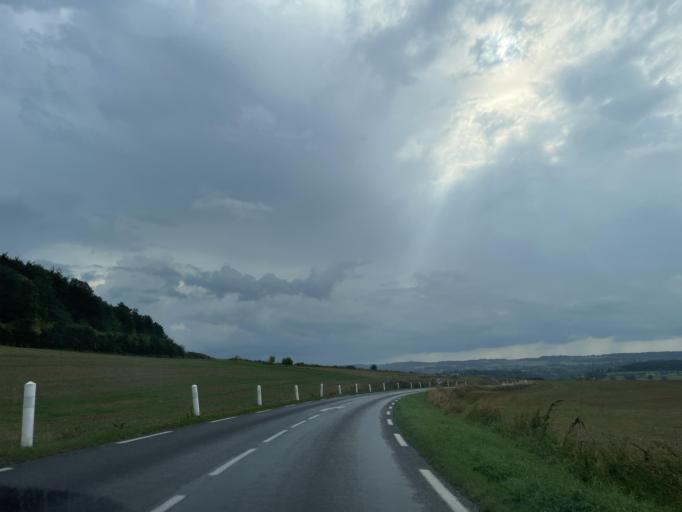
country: FR
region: Haute-Normandie
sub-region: Departement de la Seine-Maritime
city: Neufchatel-en-Bray
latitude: 49.7492
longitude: 1.4338
